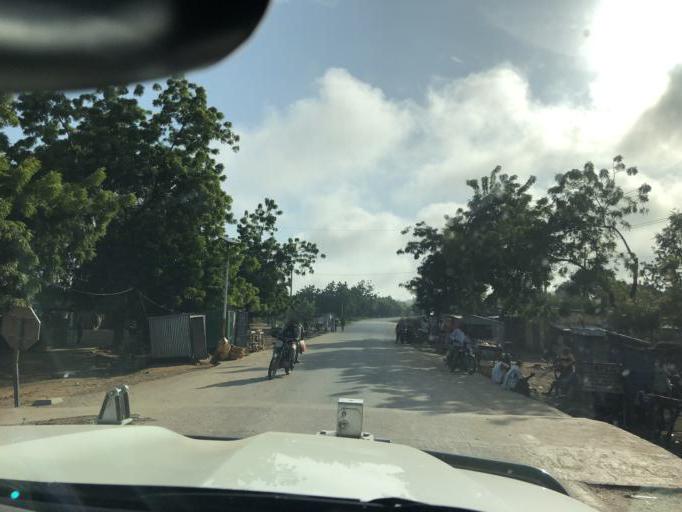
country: CM
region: North Province
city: Pitoa
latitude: 9.4936
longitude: 13.6830
